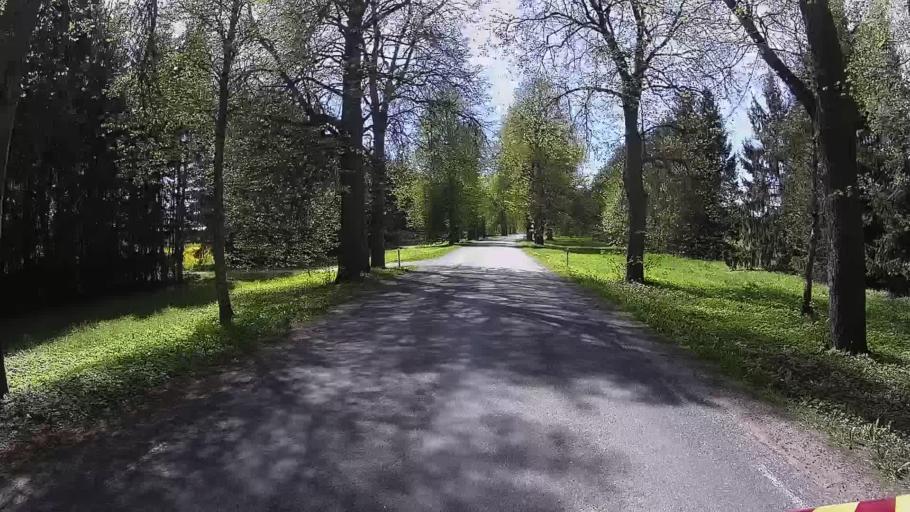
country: LV
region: Apes Novads
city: Ape
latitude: 57.6174
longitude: 26.5886
